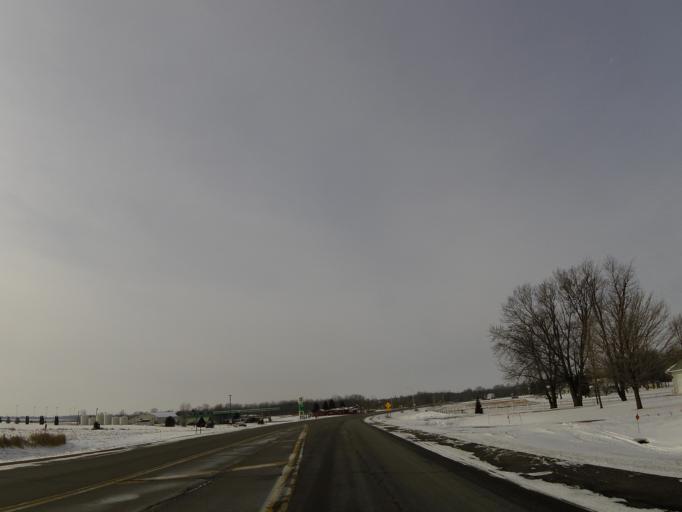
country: US
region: Minnesota
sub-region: McLeod County
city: Lester Prairie
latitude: 44.9053
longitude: -93.9663
